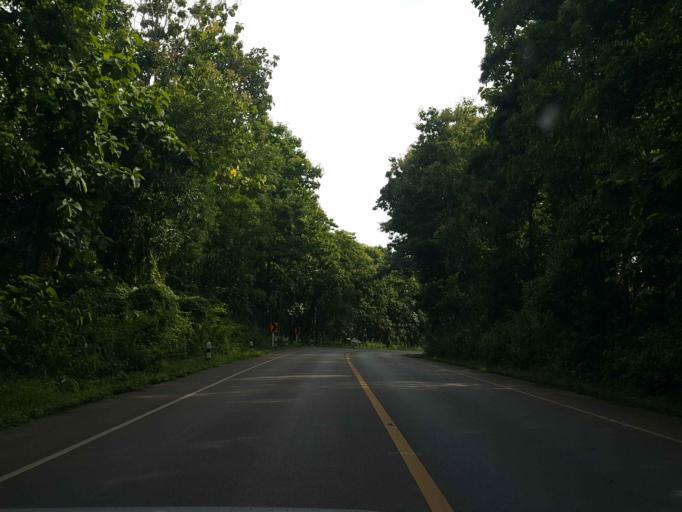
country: TH
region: Phrae
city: Den Chai
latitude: 17.8375
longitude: 99.8726
